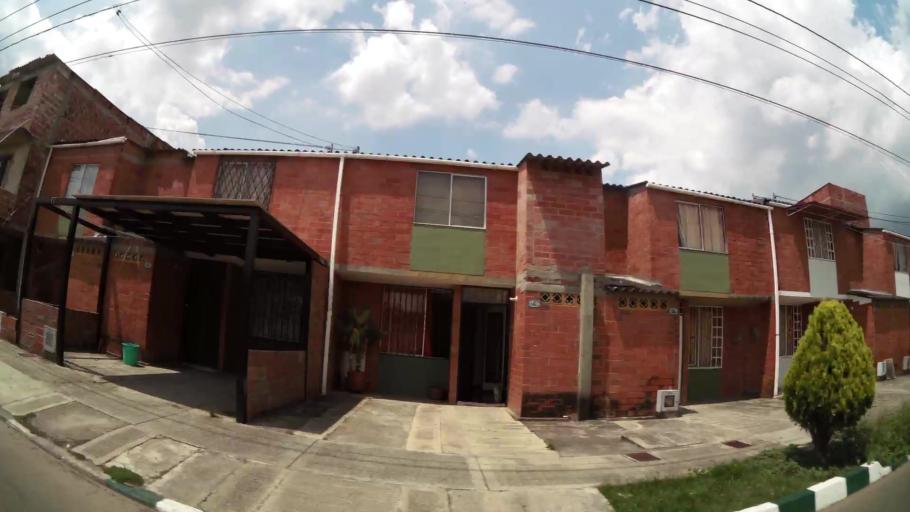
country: CO
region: Valle del Cauca
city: Cali
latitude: 3.4558
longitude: -76.4619
